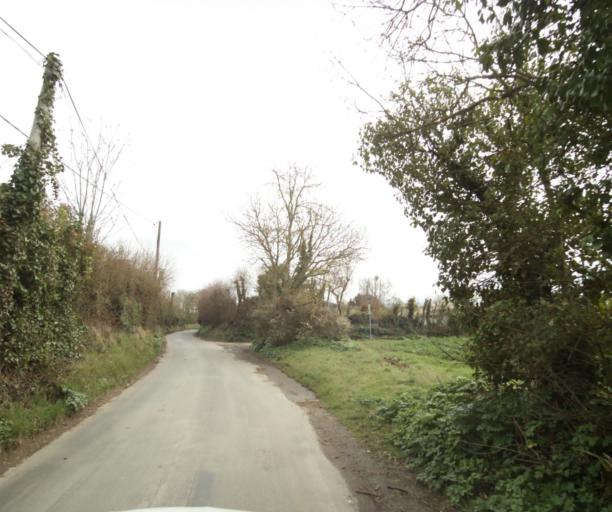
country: FR
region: Poitou-Charentes
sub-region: Departement de la Charente-Maritime
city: Lagord
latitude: 46.1894
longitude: -1.1685
